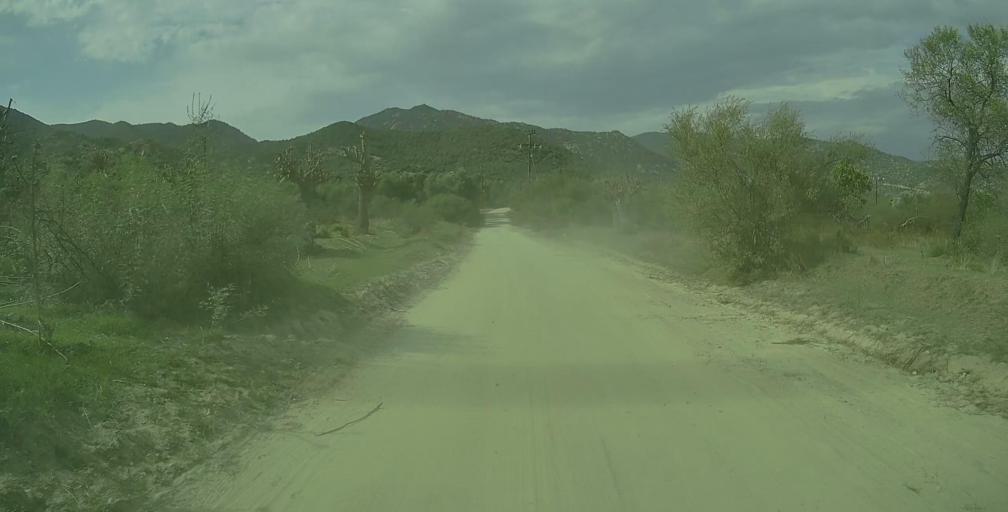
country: GR
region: Central Macedonia
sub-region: Nomos Chalkidikis
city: Sykia
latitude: 40.0265
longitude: 23.9462
